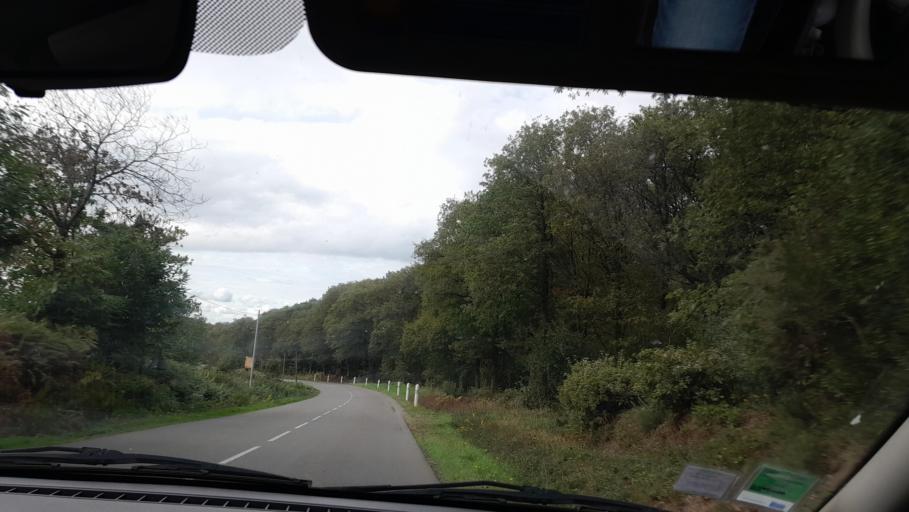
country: FR
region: Brittany
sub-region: Departement d'Ille-et-Vilaine
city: Le Pertre
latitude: 48.0453
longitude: -1.0844
